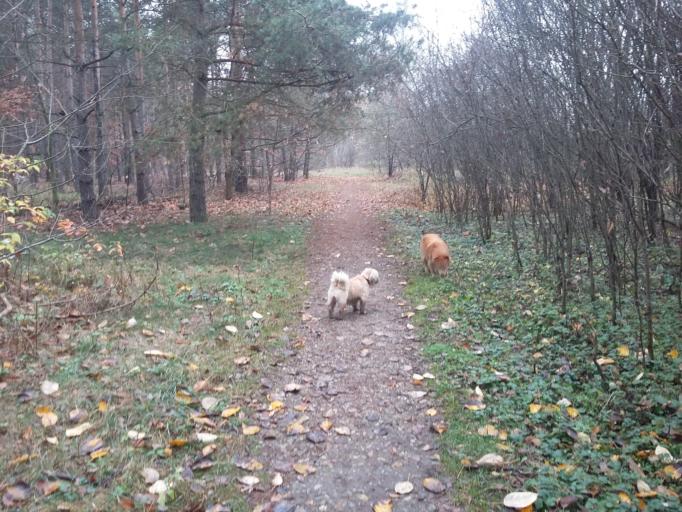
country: PL
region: Lodz Voivodeship
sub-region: Powiat pabianicki
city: Ksawerow
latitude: 51.7234
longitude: 19.3871
